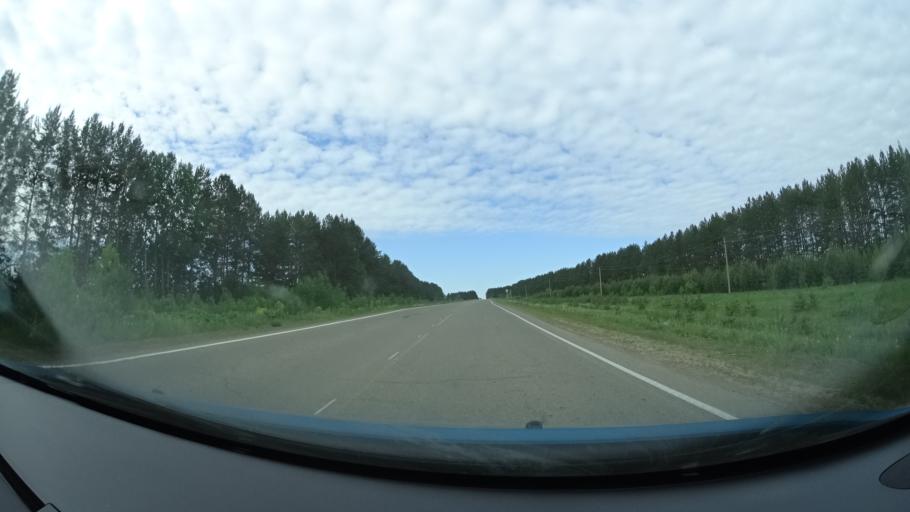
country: RU
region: Perm
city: Kuyeda
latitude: 56.4844
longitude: 55.5968
